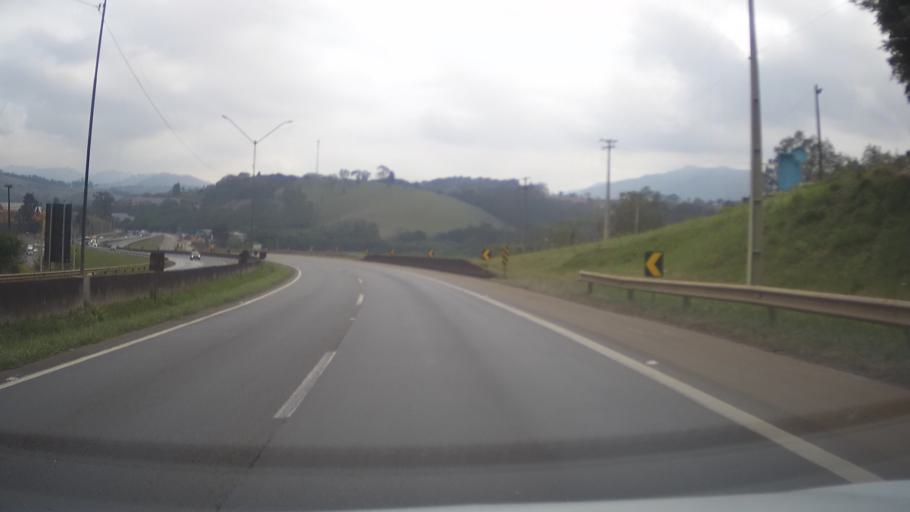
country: BR
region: Minas Gerais
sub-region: Extrema
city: Extrema
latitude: -22.8345
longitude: -46.3187
